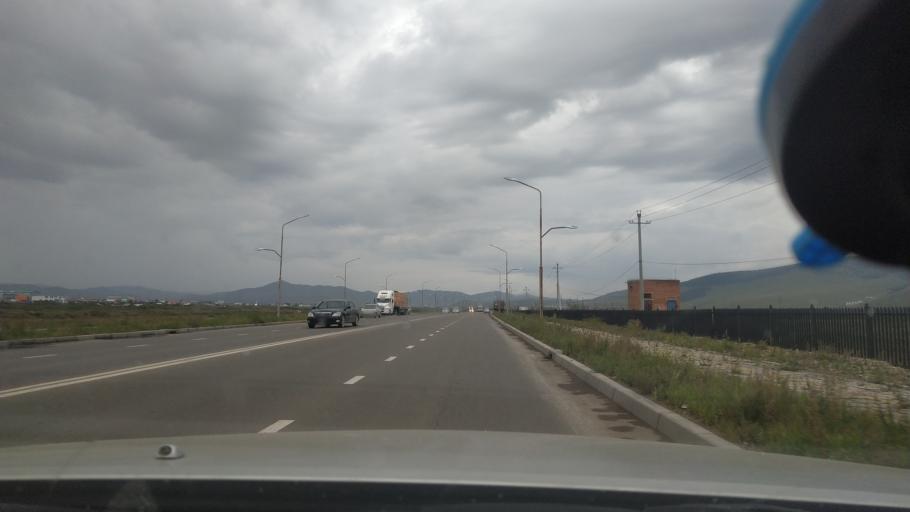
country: MN
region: Ulaanbaatar
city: Ulaanbaatar
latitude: 47.9037
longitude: 106.9784
